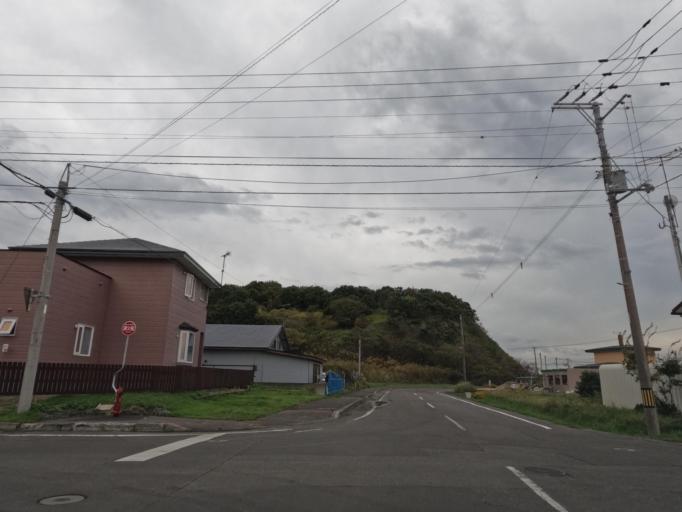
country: JP
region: Hokkaido
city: Date
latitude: 42.3929
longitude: 140.9087
